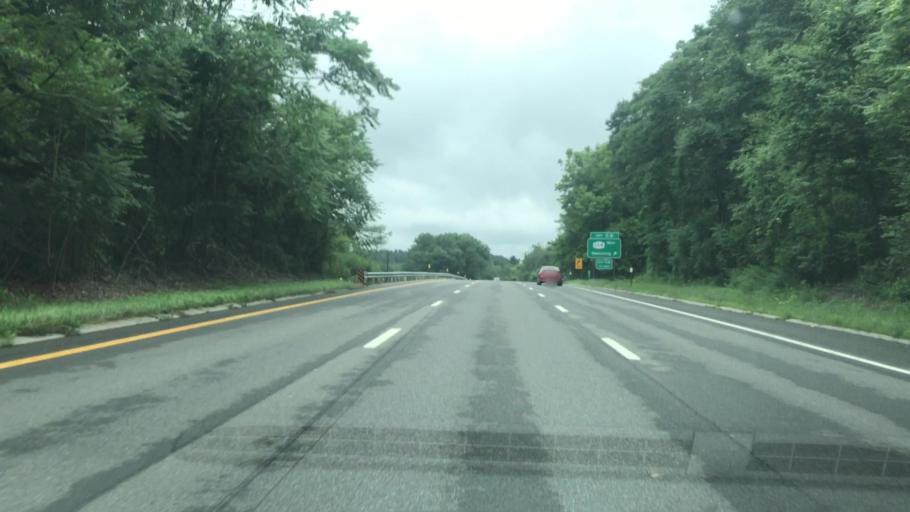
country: US
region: New York
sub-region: Westchester County
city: Yorktown Heights
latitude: 41.2176
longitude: -73.8115
